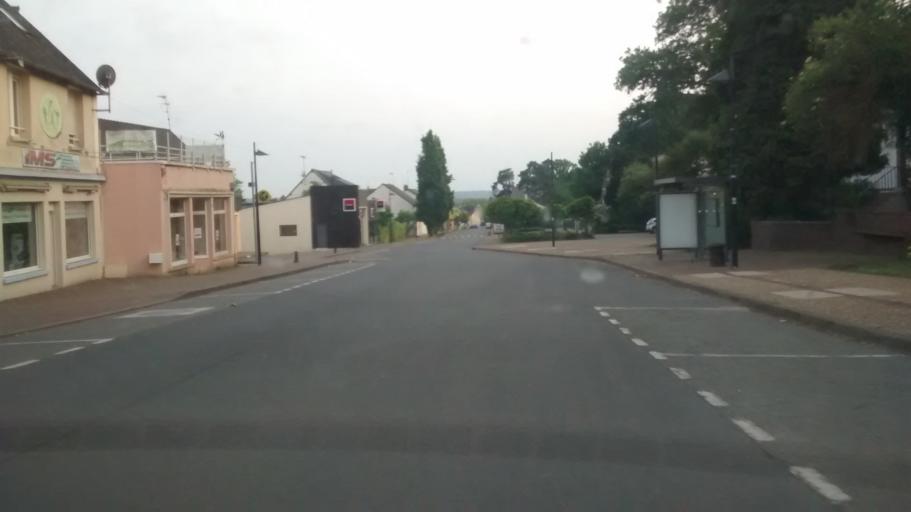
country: FR
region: Brittany
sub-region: Departement du Morbihan
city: Guer
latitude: 47.9428
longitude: -2.1316
